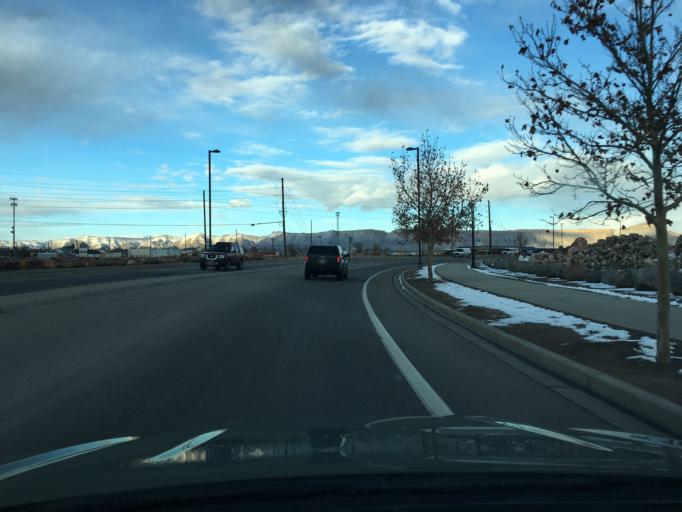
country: US
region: Colorado
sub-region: Mesa County
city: Grand Junction
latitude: 39.0619
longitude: -108.5456
